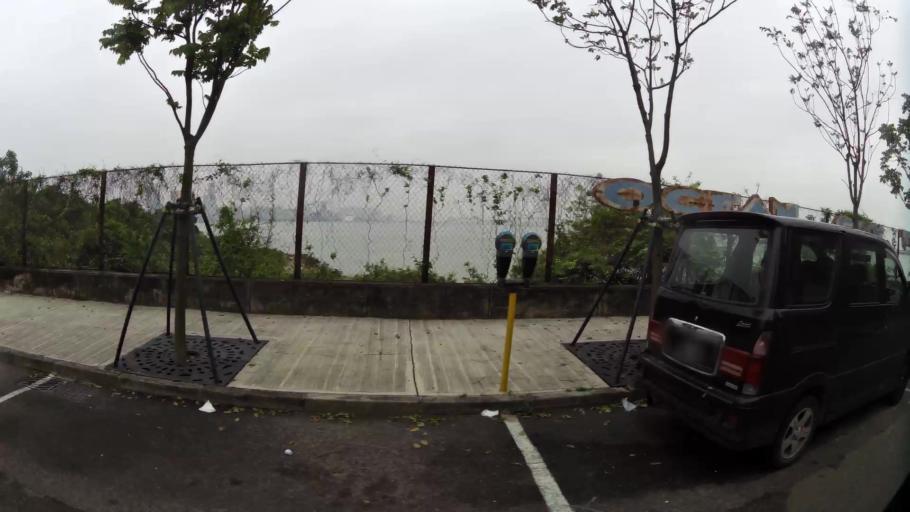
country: MO
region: Macau
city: Macau
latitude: 22.1659
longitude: 113.5570
